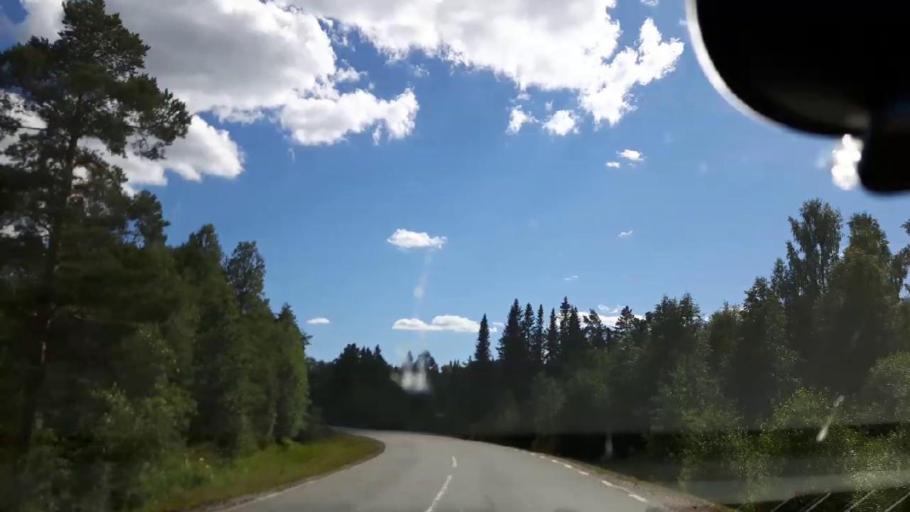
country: SE
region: Jaemtland
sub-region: Ragunda Kommun
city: Hammarstrand
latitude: 62.8348
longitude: 16.1748
